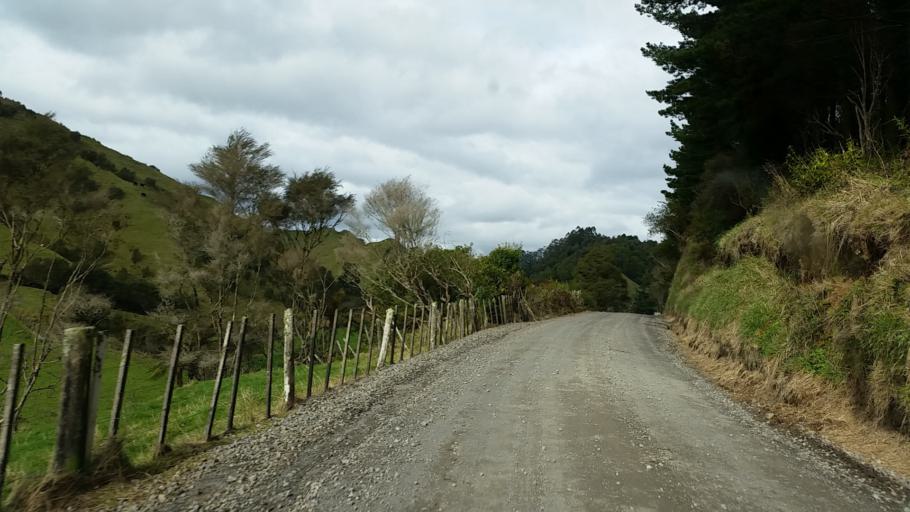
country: NZ
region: Taranaki
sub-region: New Plymouth District
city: Waitara
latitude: -39.1563
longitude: 174.5608
